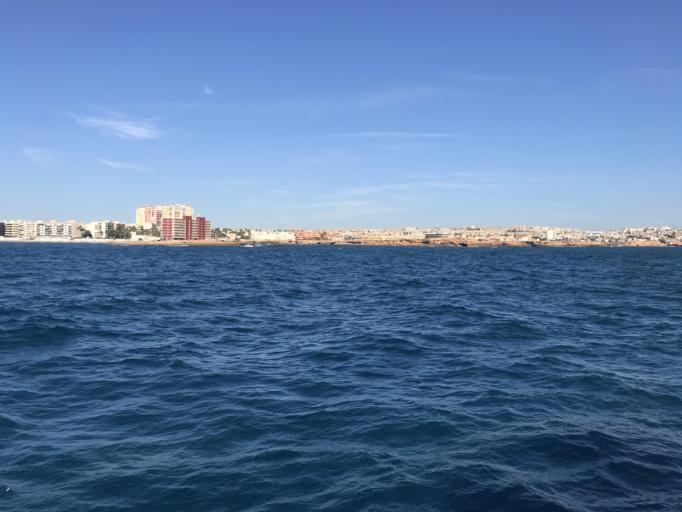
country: ES
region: Valencia
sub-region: Provincia de Alicante
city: Torrevieja
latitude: 37.9805
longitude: -0.6523
